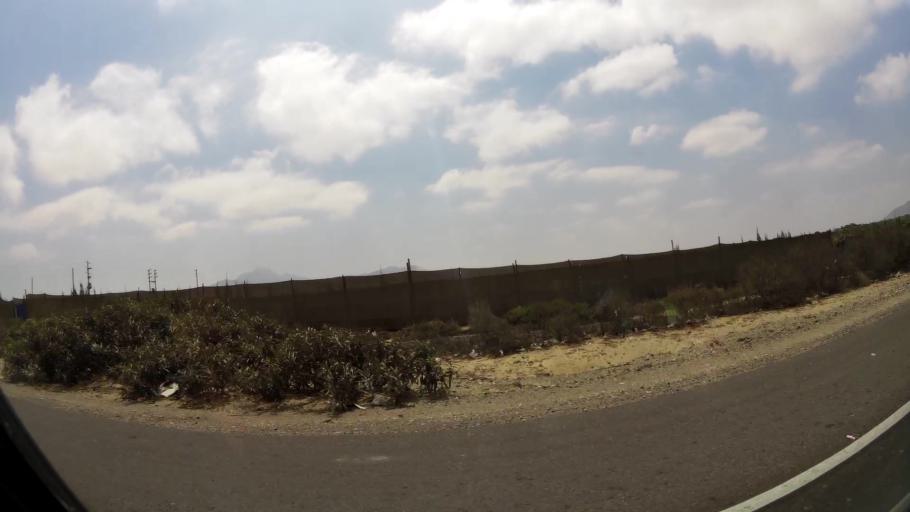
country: PE
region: La Libertad
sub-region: Ascope
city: Paijan
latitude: -7.6598
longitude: -79.3361
